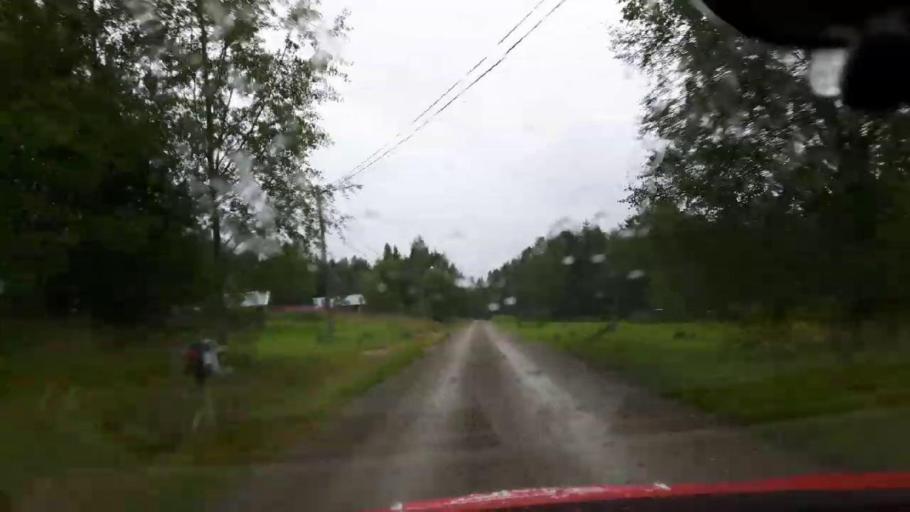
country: SE
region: Jaemtland
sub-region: OEstersunds Kommun
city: Brunflo
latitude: 62.7903
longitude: 14.9641
